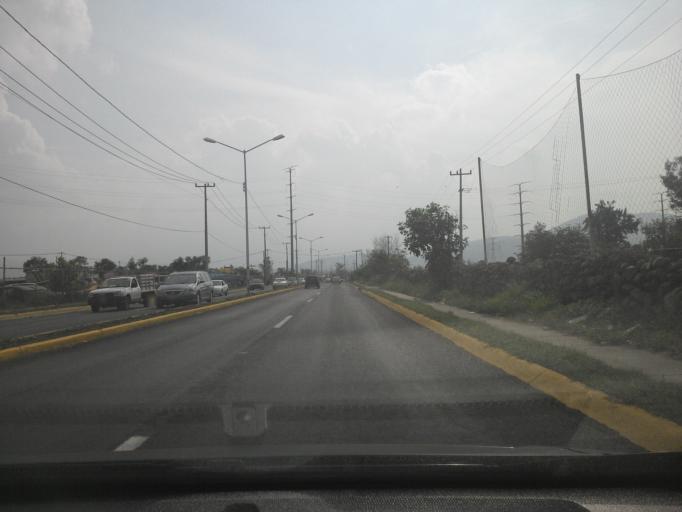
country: MX
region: Jalisco
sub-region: Tlajomulco de Zuniga
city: Villas de la Hacienda [Fraccionamiento]
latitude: 20.5432
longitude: -103.4026
